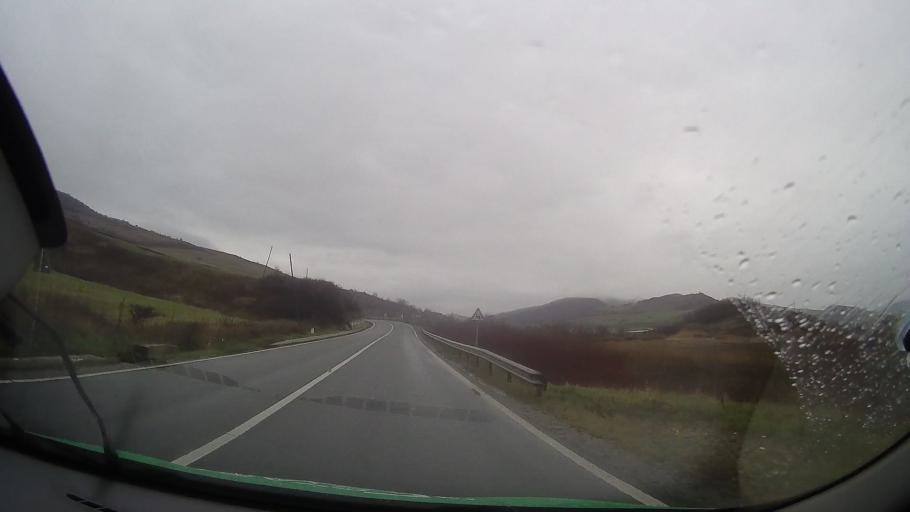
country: RO
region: Bistrita-Nasaud
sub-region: Comuna Galatii Bistritei
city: Galatii Bistritei
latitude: 46.9536
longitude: 24.4461
